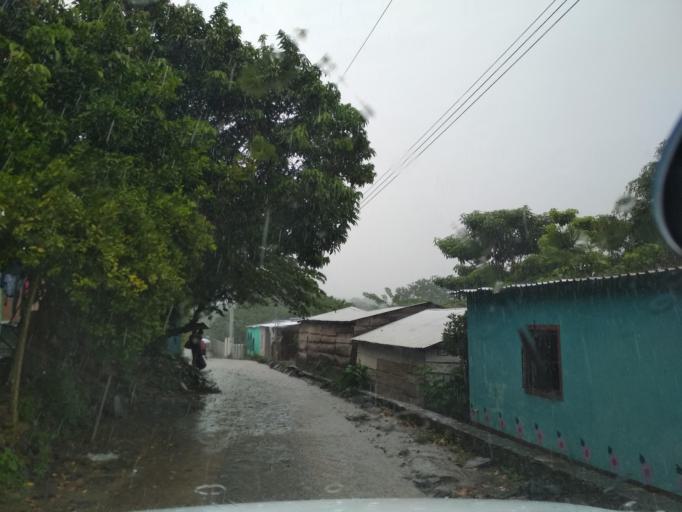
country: MX
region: Veracruz
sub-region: San Andres Tuxtla
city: Soyata
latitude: 18.4105
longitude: -95.2991
